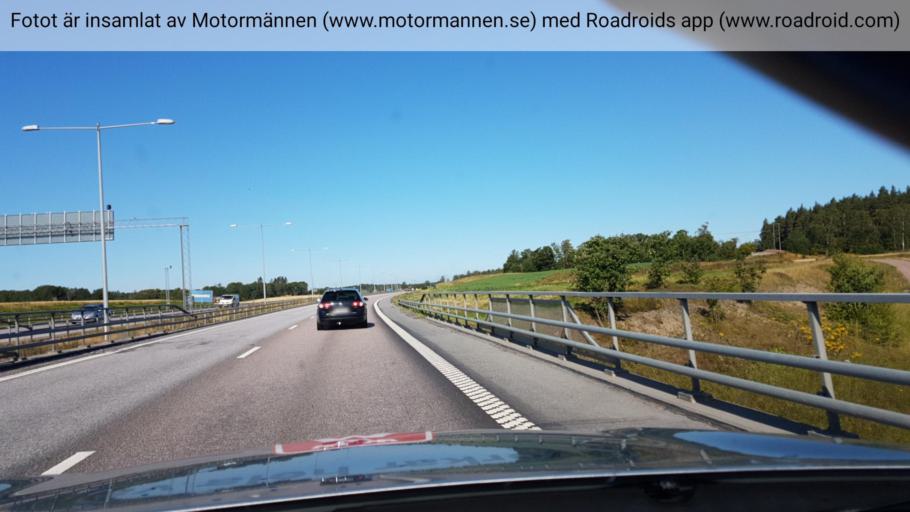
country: SE
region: Stockholm
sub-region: Taby Kommun
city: Taby
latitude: 59.4745
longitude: 18.0350
